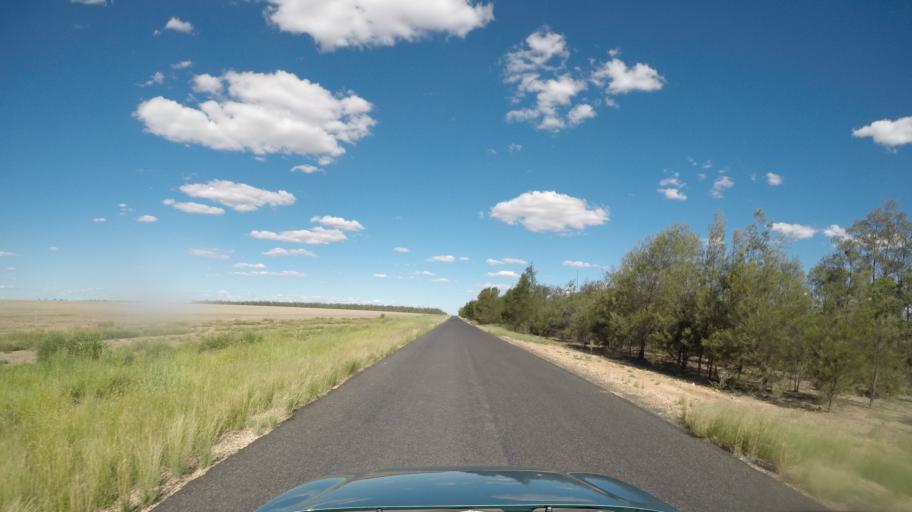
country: AU
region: Queensland
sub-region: Goondiwindi
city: Goondiwindi
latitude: -28.1714
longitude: 150.2222
